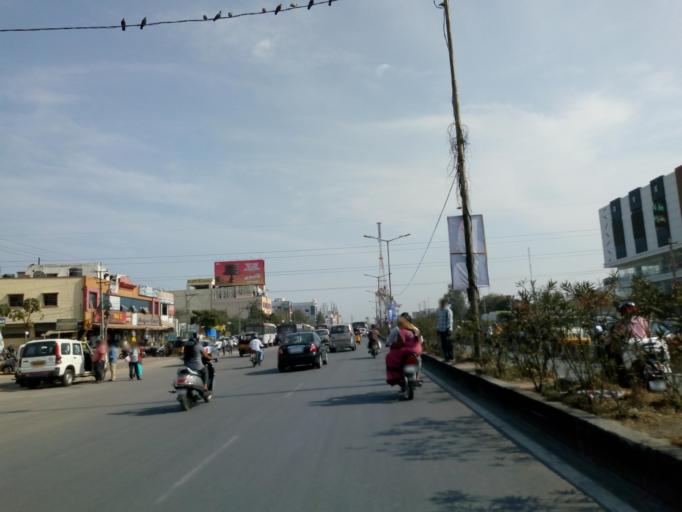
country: IN
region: Telangana
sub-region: Rangareddi
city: Lal Bahadur Nagar
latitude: 17.3446
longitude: 78.5539
